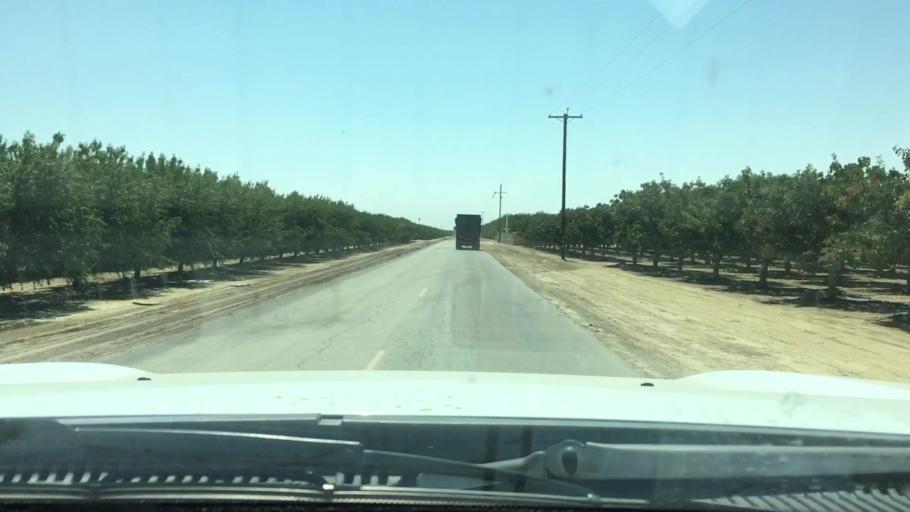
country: US
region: California
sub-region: Kern County
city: Wasco
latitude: 35.5239
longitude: -119.4032
